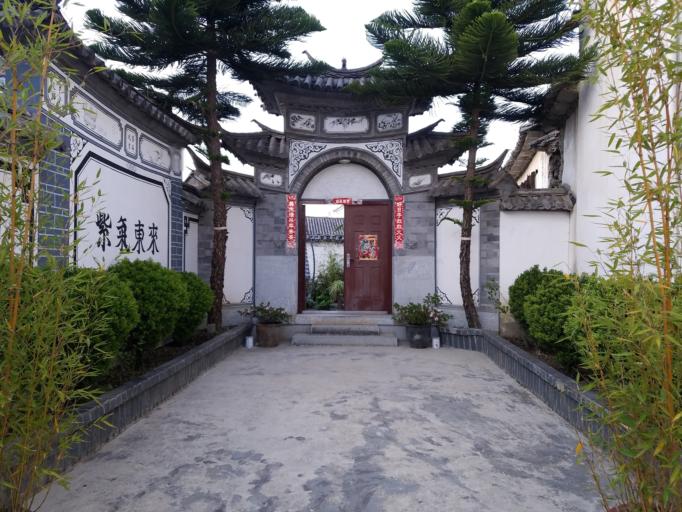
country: CN
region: Yunnan
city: Shangjie
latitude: 25.8237
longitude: 100.1458
